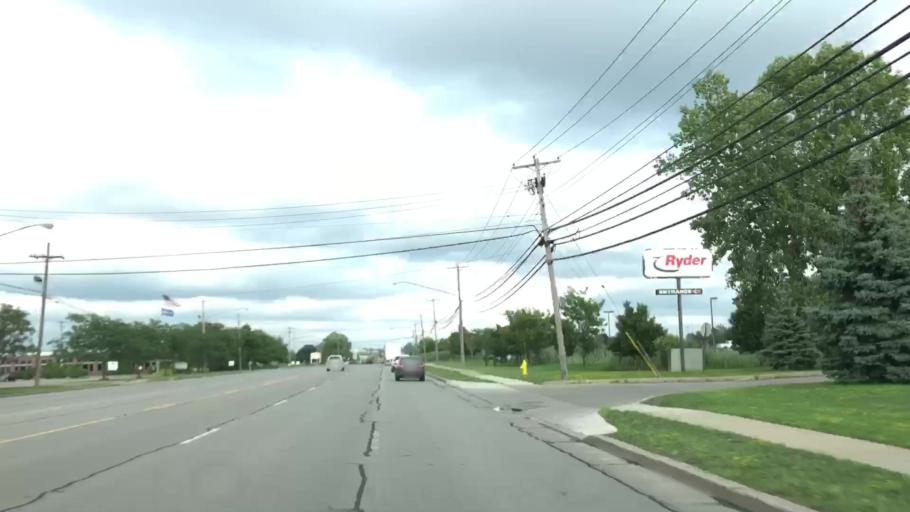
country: US
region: New York
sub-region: Erie County
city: Cheektowaga
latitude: 42.9091
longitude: -78.7355
